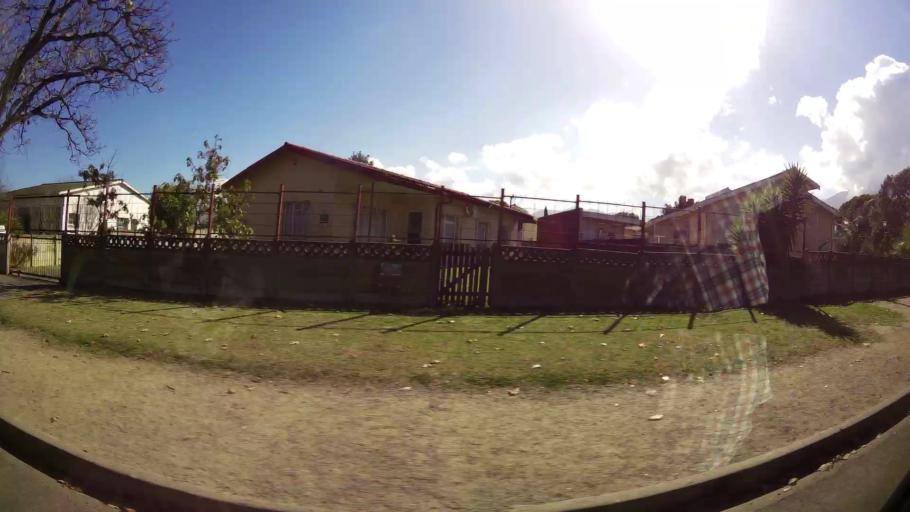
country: ZA
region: Western Cape
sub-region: Eden District Municipality
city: George
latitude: -33.9688
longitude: 22.4532
